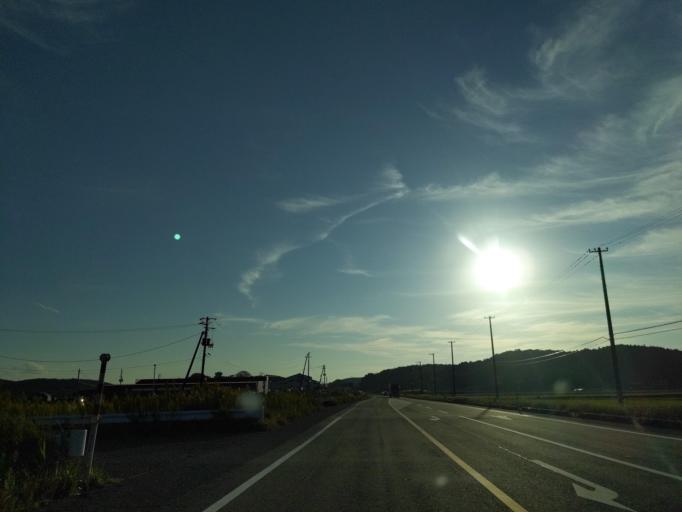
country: JP
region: Niigata
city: Nagaoka
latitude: 37.5748
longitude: 138.7479
